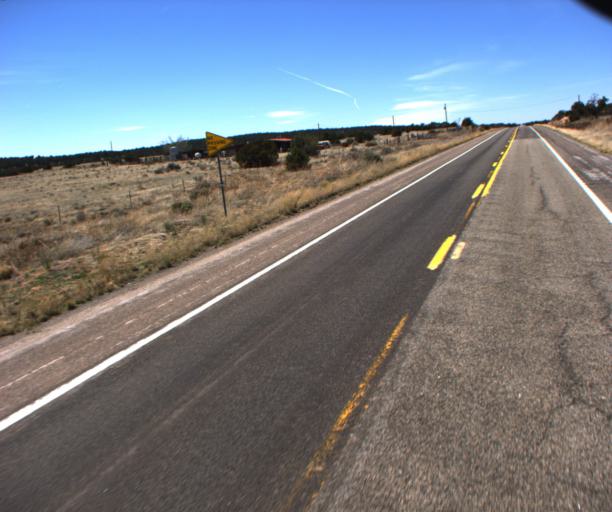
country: US
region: Arizona
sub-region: Mohave County
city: Peach Springs
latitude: 35.4996
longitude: -113.1710
